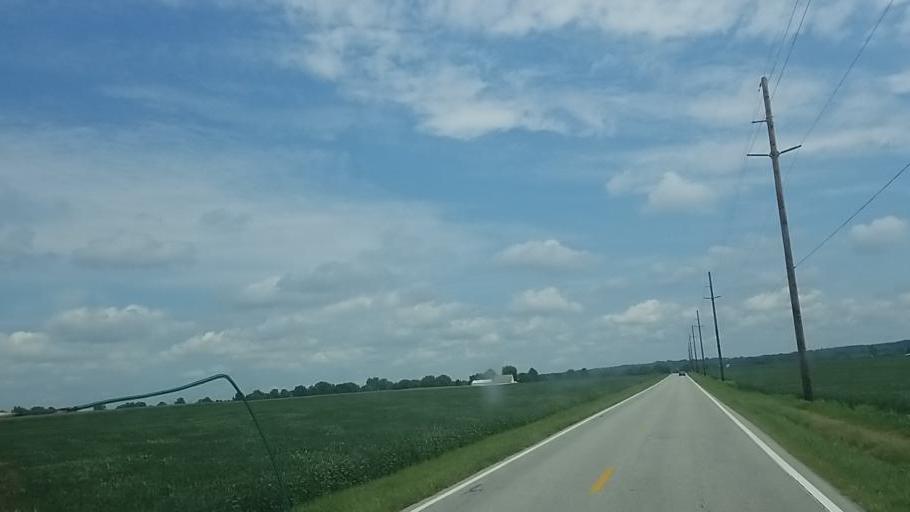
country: US
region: Ohio
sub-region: Fairfield County
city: Lithopolis
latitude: 39.7979
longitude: -82.8797
